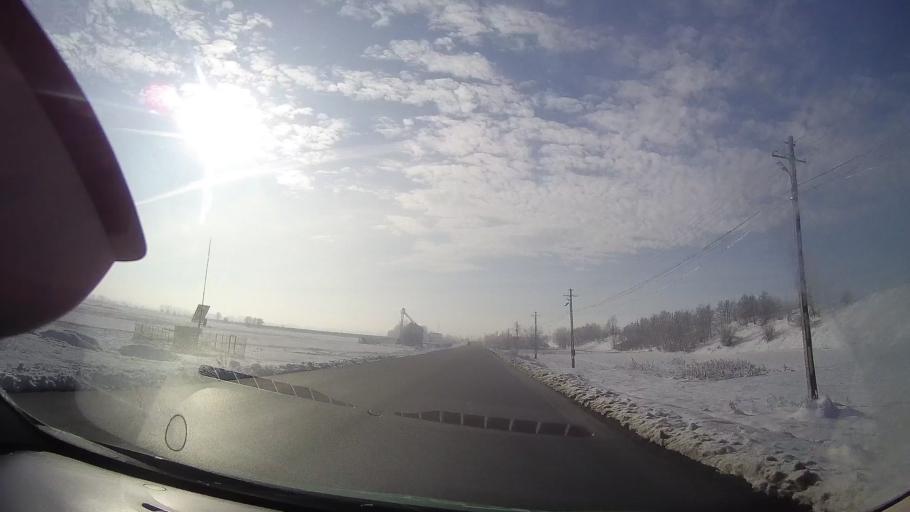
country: RO
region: Iasi
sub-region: Comuna Cristesti
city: Cristesti
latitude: 47.2533
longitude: 26.5523
